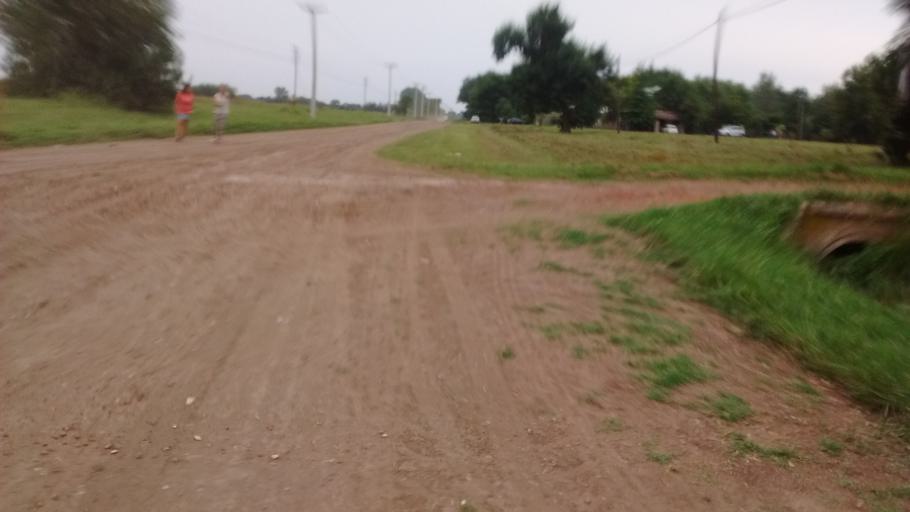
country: AR
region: Santa Fe
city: Funes
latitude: -32.9131
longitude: -60.8341
